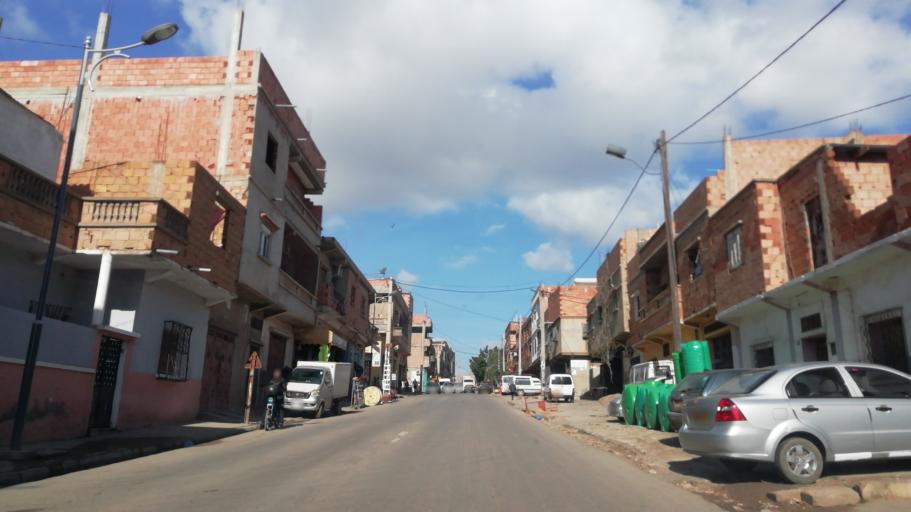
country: DZ
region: Oran
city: Es Senia
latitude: 35.6356
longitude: -0.6633
